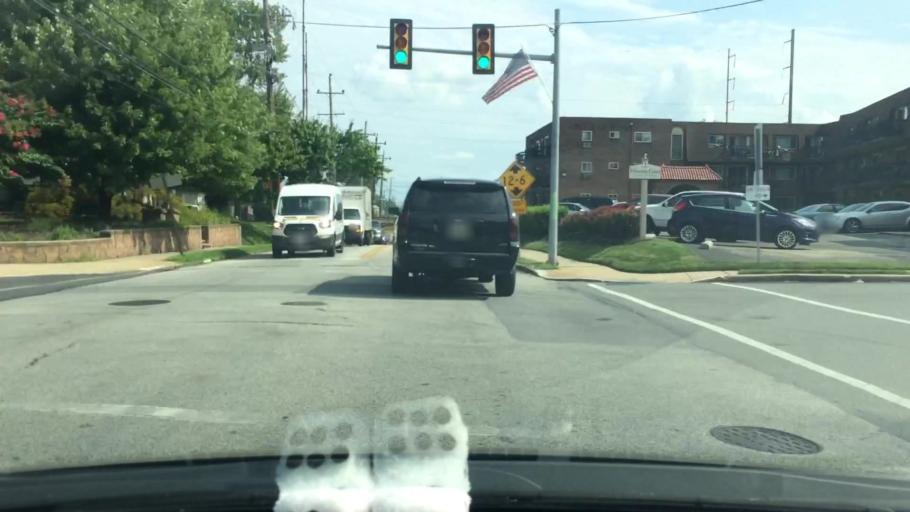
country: US
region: Pennsylvania
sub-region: Delaware County
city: Prospect Park
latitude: 39.8890
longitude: -75.3110
